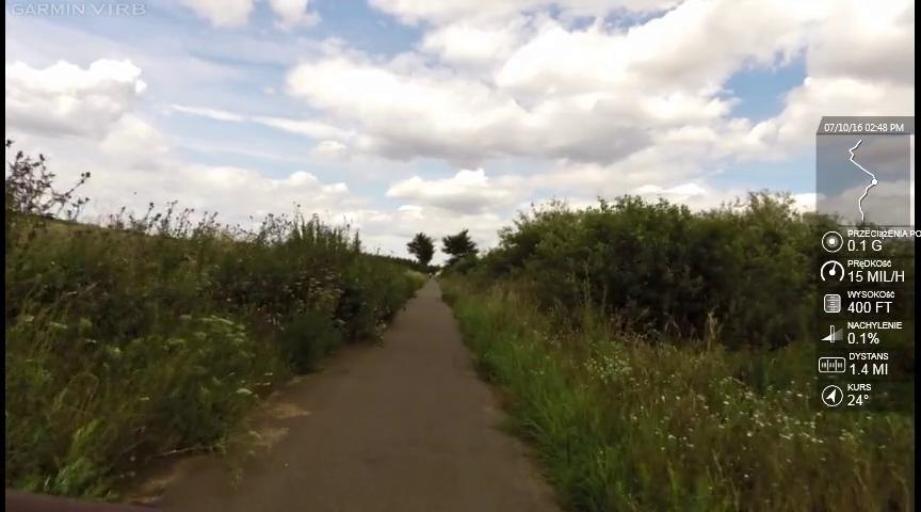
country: PL
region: West Pomeranian Voivodeship
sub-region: Powiat gryfinski
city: Banie
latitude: 53.0937
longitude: 14.6494
